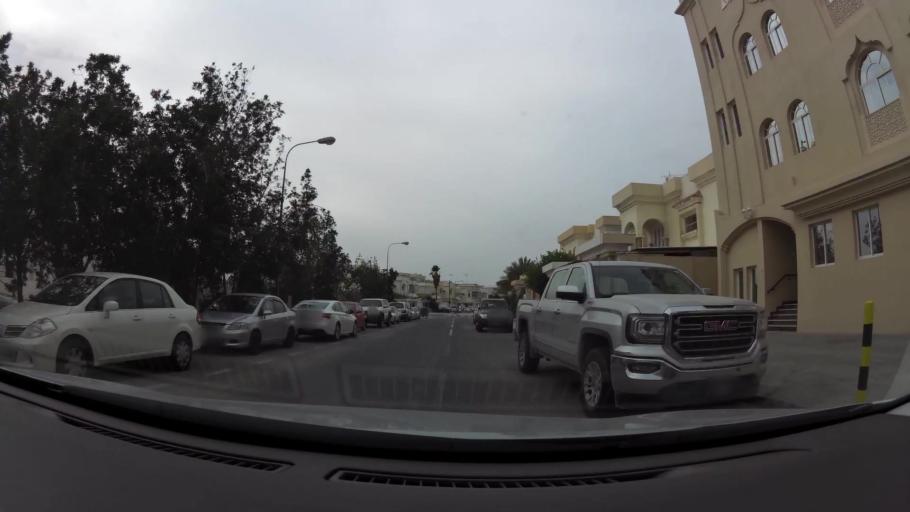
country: QA
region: Baladiyat ad Dawhah
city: Doha
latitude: 25.3098
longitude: 51.4890
